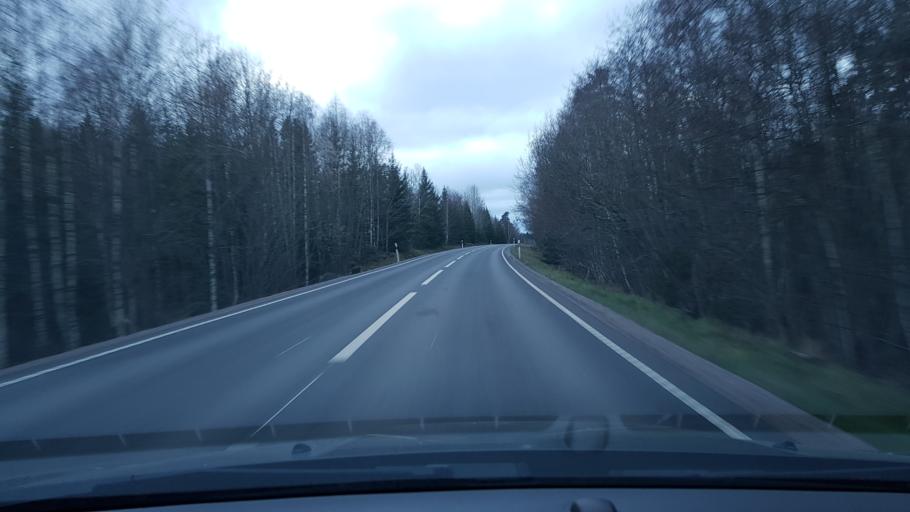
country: SE
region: Uppsala
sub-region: Osthammars Kommun
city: Osterbybruk
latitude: 59.9462
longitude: 17.9972
